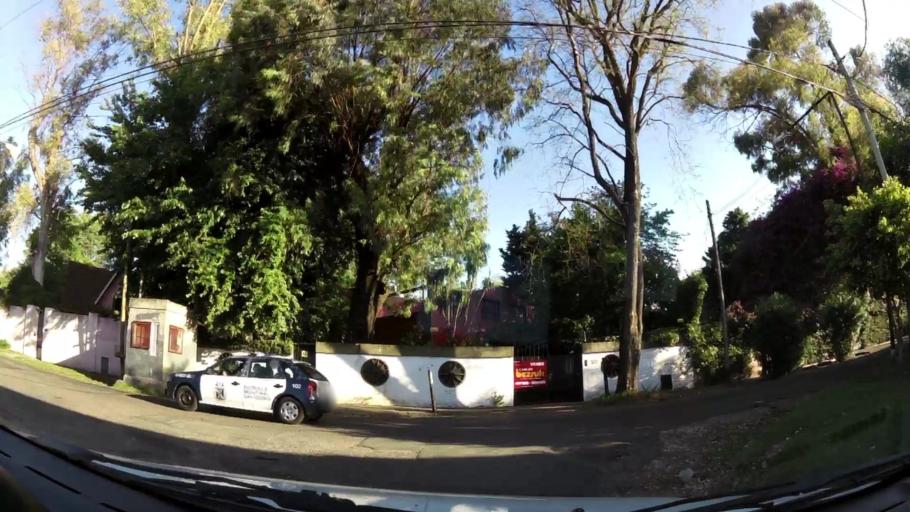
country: AR
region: Buenos Aires
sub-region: Partido de San Isidro
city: San Isidro
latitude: -34.4758
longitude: -58.5521
